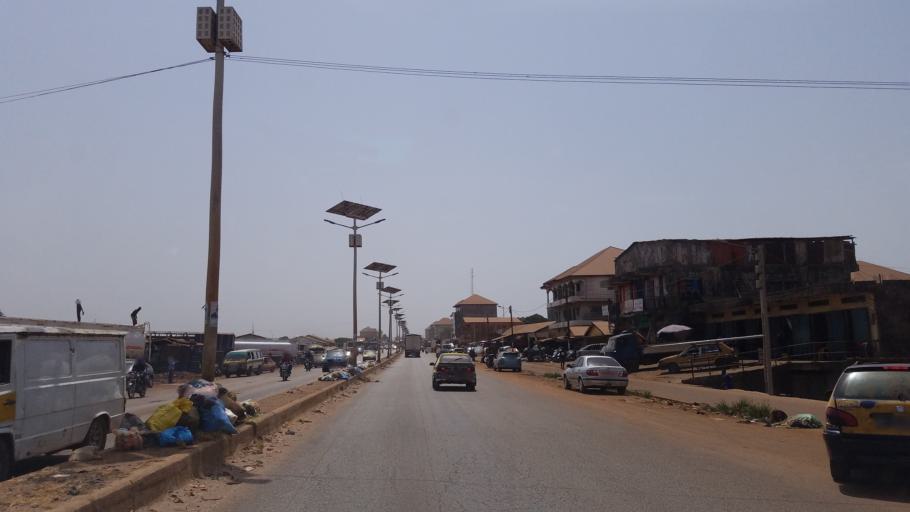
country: GN
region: Kindia
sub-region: Prefecture de Dubreka
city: Dubreka
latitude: 9.6564
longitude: -13.5707
